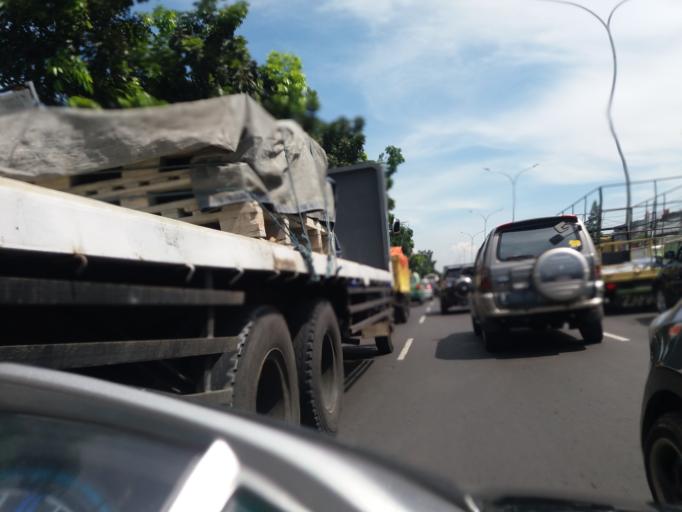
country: ID
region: West Java
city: Bandung
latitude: -6.9470
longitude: 107.6368
